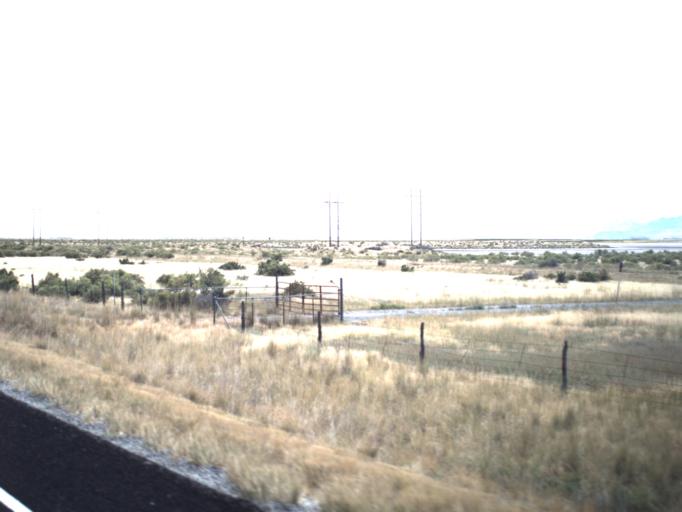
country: US
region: Utah
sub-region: Box Elder County
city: Tremonton
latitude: 41.6202
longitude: -112.3861
